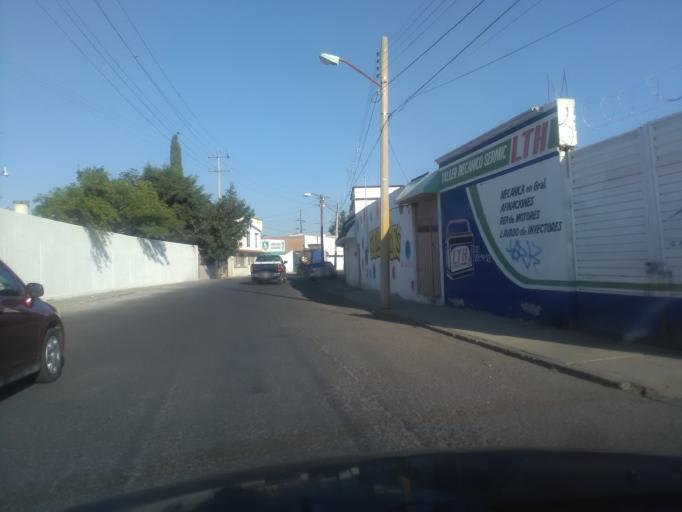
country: MX
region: Durango
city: Victoria de Durango
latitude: 24.0419
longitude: -104.6320
